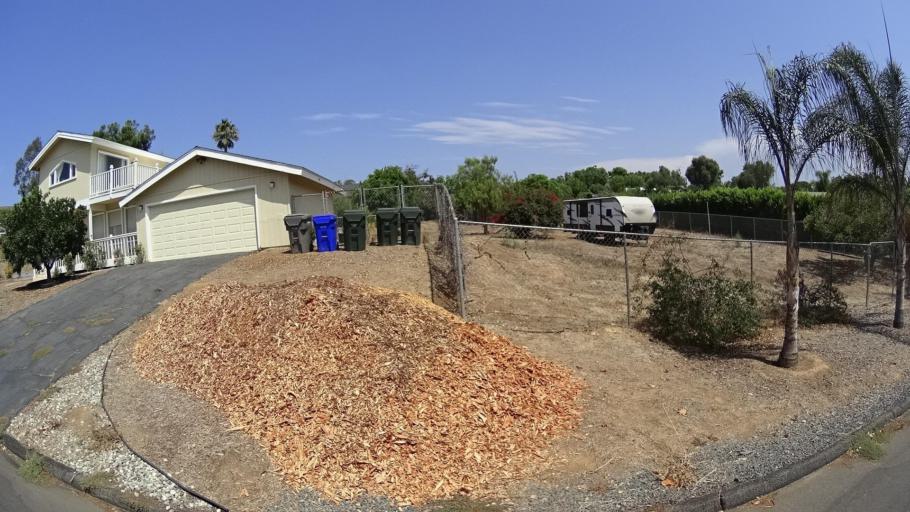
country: US
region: California
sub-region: San Diego County
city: Fallbrook
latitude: 33.3620
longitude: -117.2391
